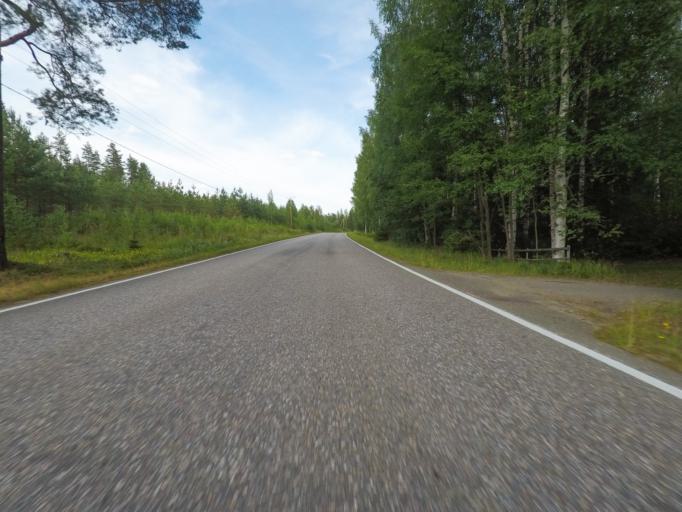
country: FI
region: Southern Savonia
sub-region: Savonlinna
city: Sulkava
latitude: 61.7508
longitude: 28.2099
